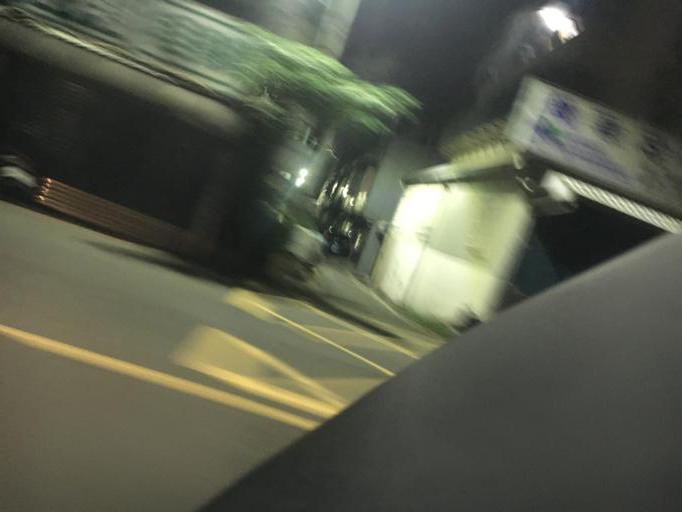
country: TW
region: Taiwan
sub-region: Hsinchu
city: Hsinchu
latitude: 24.7937
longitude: 120.9690
